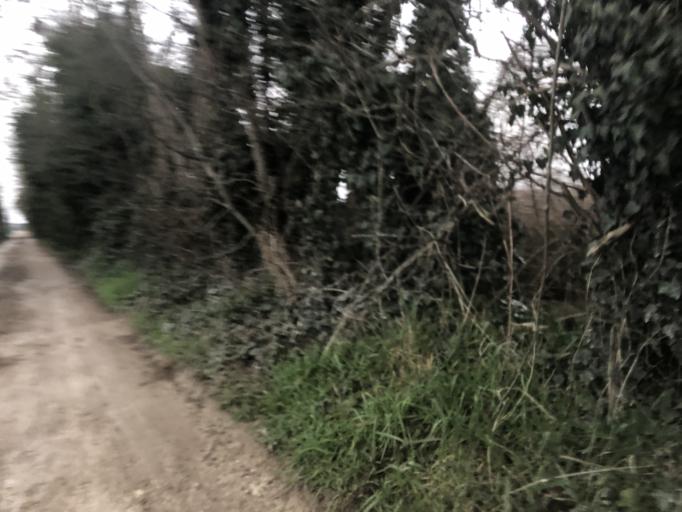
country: IT
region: Veneto
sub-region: Provincia di Verona
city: Caselle
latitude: 45.4169
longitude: 10.8904
